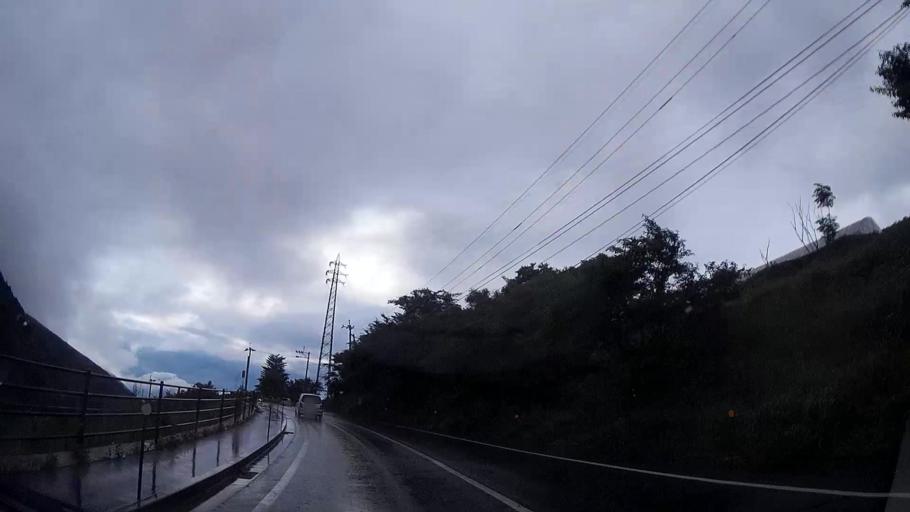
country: JP
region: Kumamoto
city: Ozu
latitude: 32.8765
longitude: 130.9775
